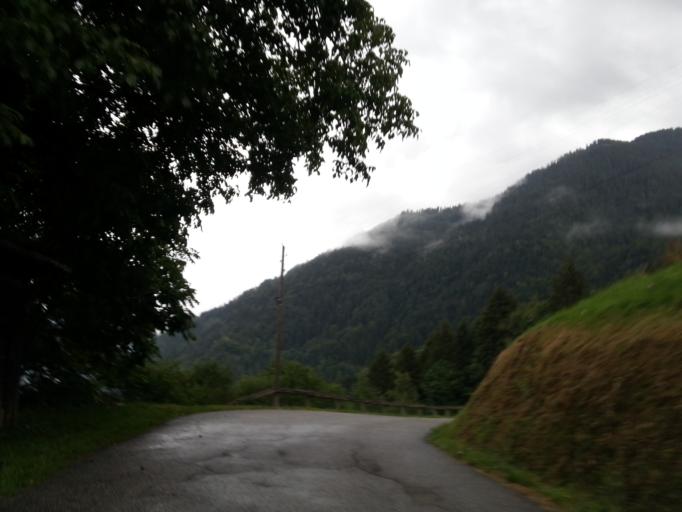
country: FR
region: Rhone-Alpes
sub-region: Departement de la Savoie
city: Marthod
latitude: 45.7072
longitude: 6.4669
